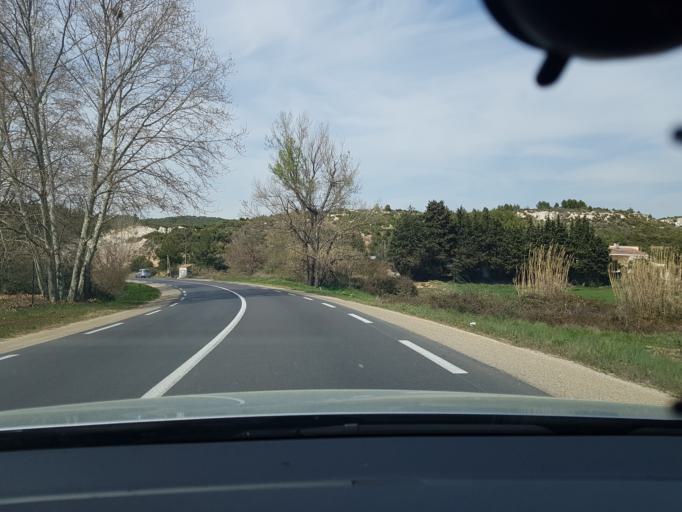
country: FR
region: Provence-Alpes-Cote d'Azur
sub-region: Departement des Bouches-du-Rhone
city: Gardanne
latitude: 43.4700
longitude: 5.4609
